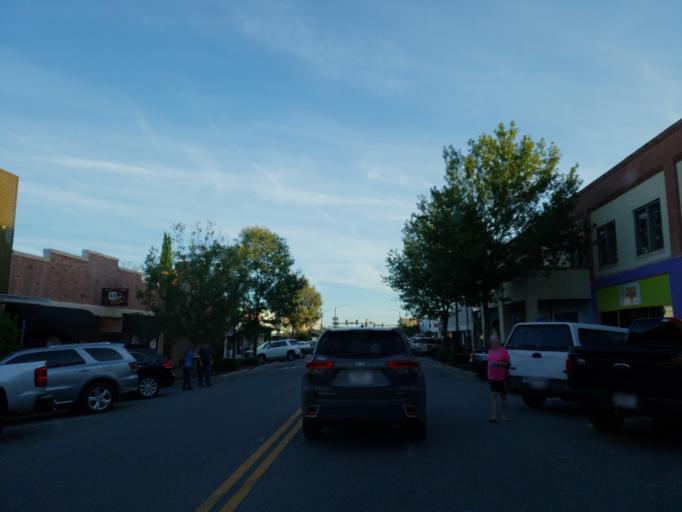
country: US
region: Georgia
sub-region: Tift County
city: Tifton
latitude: 31.4518
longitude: -83.5095
